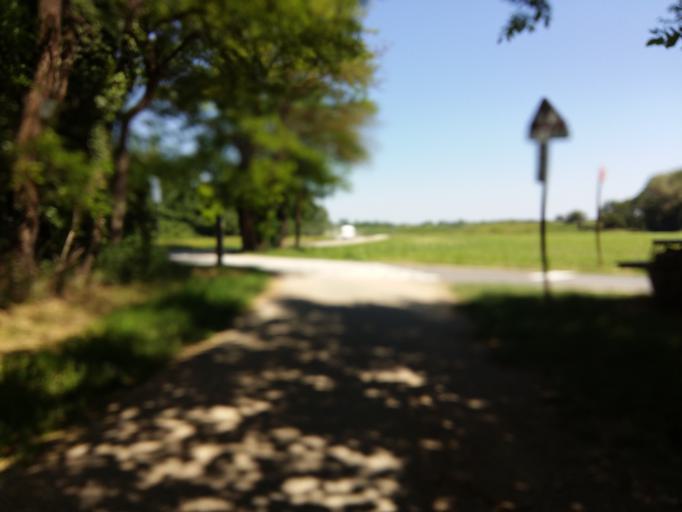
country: FR
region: Rhone-Alpes
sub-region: Departement du Rhone
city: Decines-Charpieu
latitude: 45.7936
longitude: 4.9804
